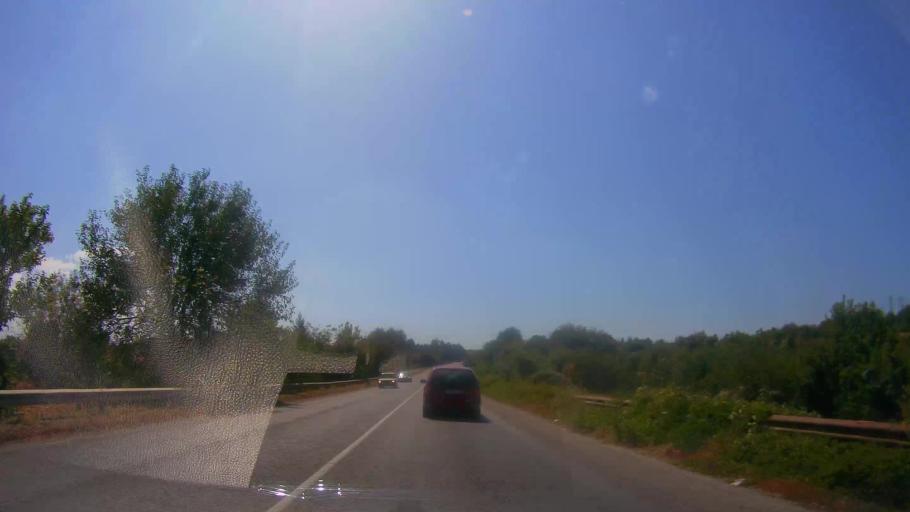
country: BG
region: Veliko Turnovo
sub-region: Obshtina Polski Trumbesh
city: Polski Trumbesh
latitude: 43.2691
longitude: 25.6436
